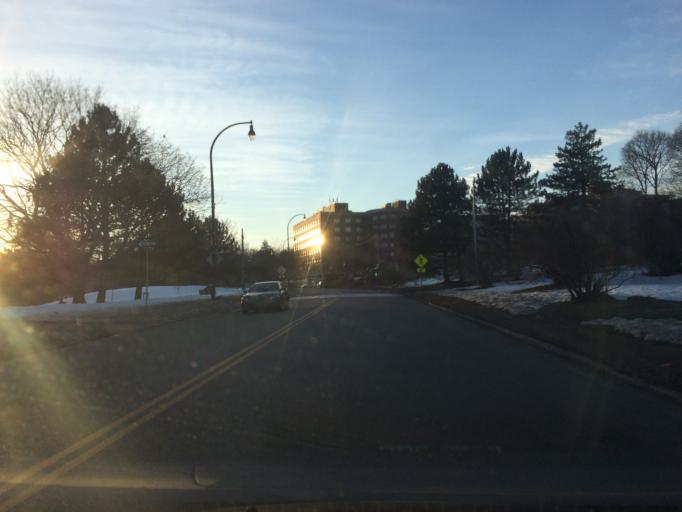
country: US
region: New York
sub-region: Monroe County
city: Rochester
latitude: 43.1294
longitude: -77.6072
